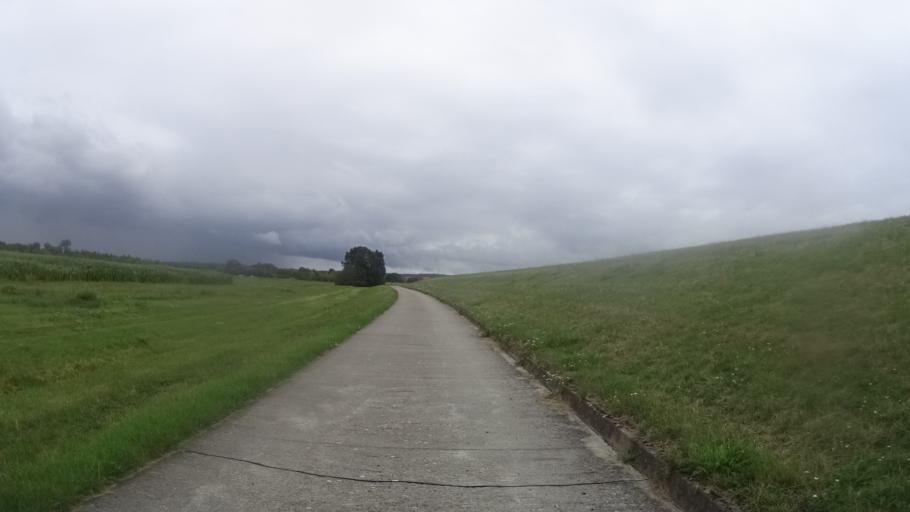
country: DE
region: Lower Saxony
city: Tosterglope
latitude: 53.2676
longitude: 10.8291
